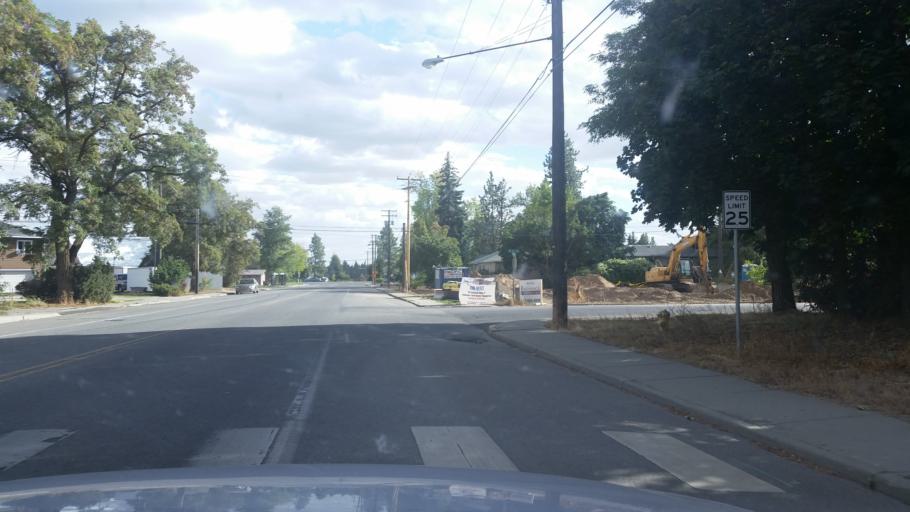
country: US
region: Washington
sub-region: Spokane County
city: Cheney
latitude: 47.4837
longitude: -117.5864
